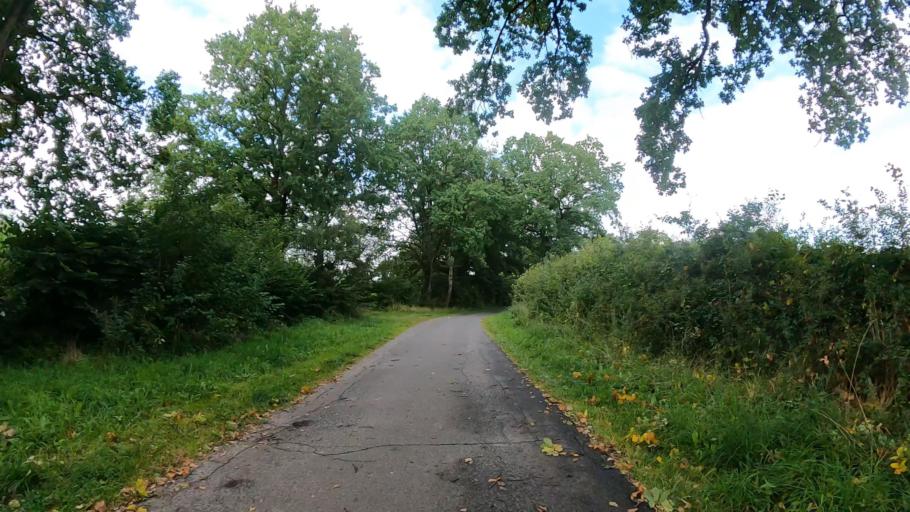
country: DE
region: Schleswig-Holstein
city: Kolln-Reisiek
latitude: 53.7306
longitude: 9.6833
